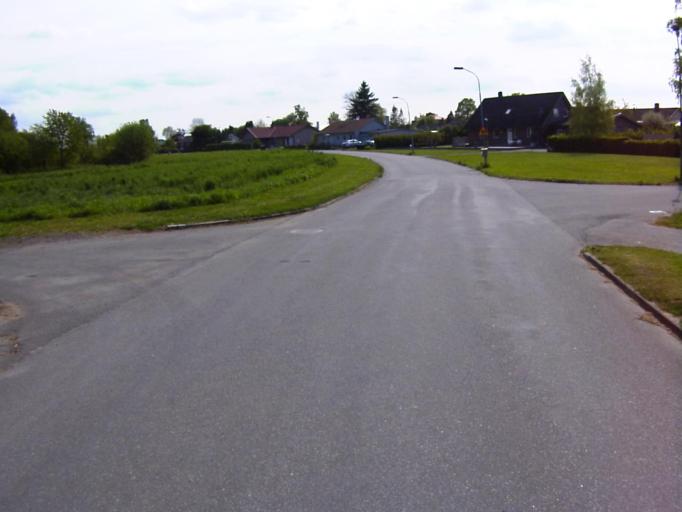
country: SE
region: Skane
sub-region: Kristianstads Kommun
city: Kristianstad
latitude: 56.0599
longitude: 14.0883
